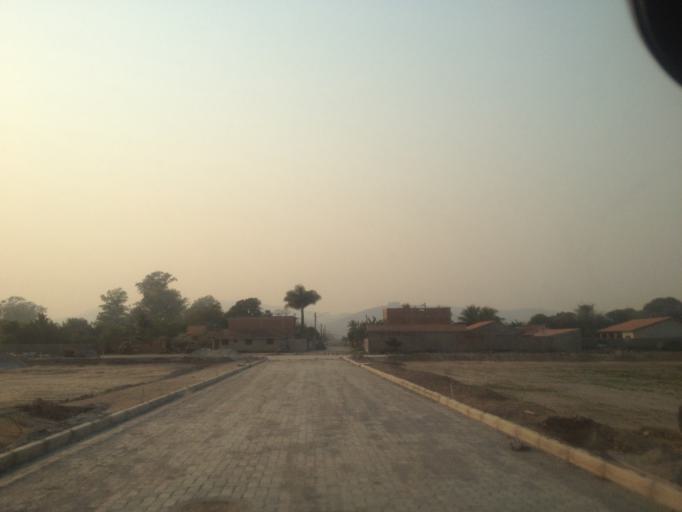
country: BR
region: Rio de Janeiro
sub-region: Porto Real
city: Porto Real
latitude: -22.4222
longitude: -44.2947
